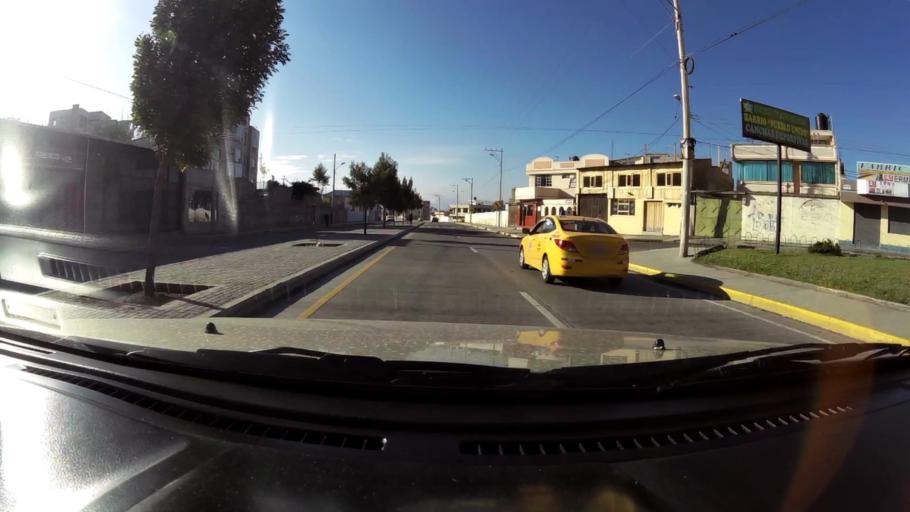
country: EC
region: Chimborazo
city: Riobamba
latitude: -1.6679
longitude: -78.6381
